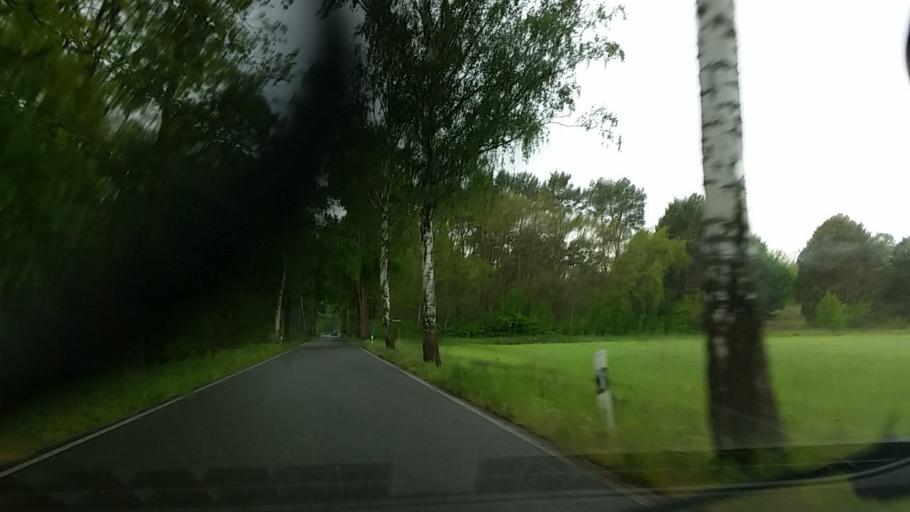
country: DE
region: Brandenburg
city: Diensdorf-Radlow
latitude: 52.2548
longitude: 14.0391
